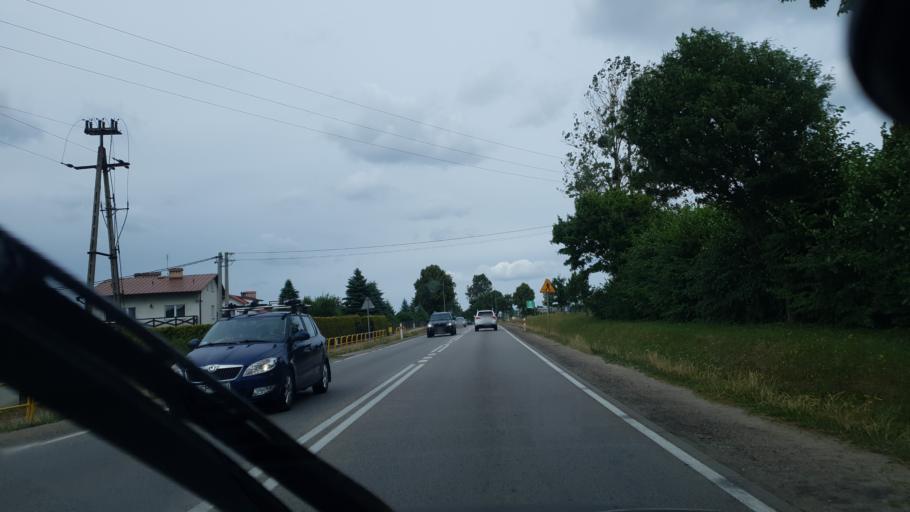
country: PL
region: Pomeranian Voivodeship
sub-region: Powiat kartuski
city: Banino
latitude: 54.4013
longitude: 18.3601
